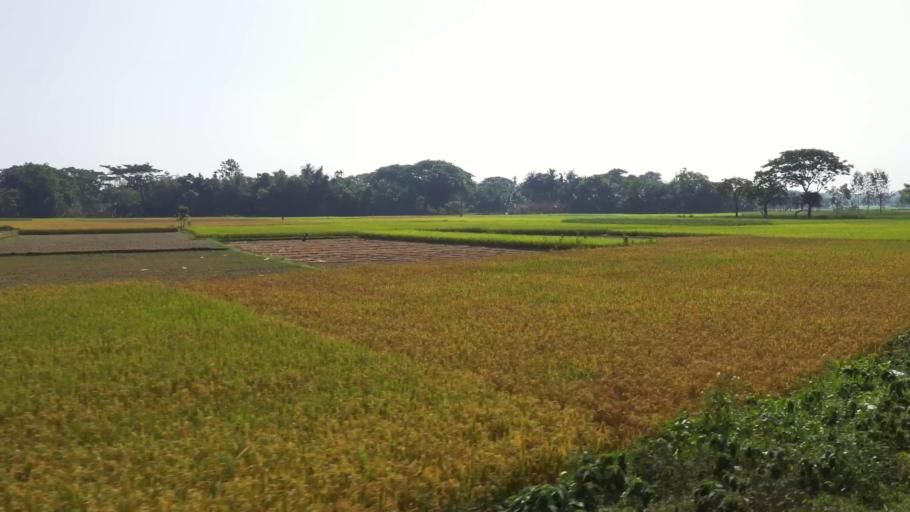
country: BD
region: Dhaka
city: Gafargaon
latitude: 24.5769
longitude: 90.5080
